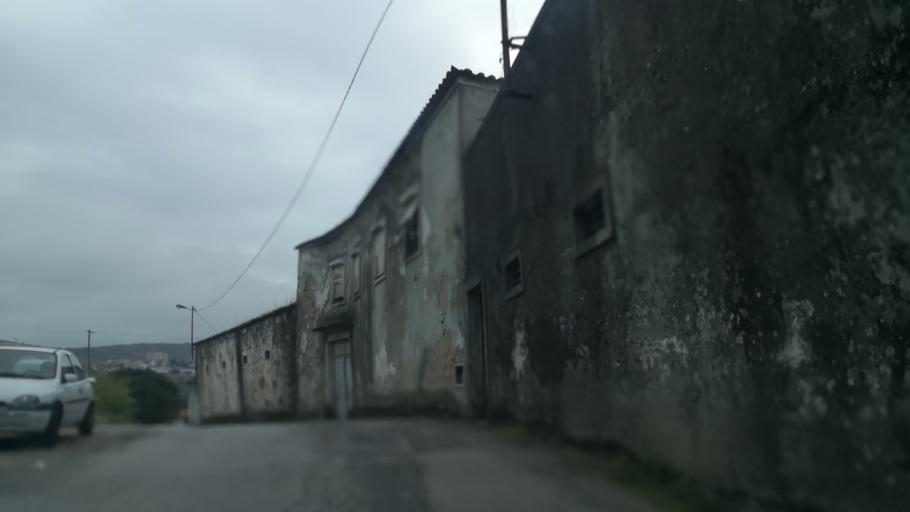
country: PT
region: Vila Real
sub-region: Peso da Regua
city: Godim
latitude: 41.1650
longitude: -7.8033
